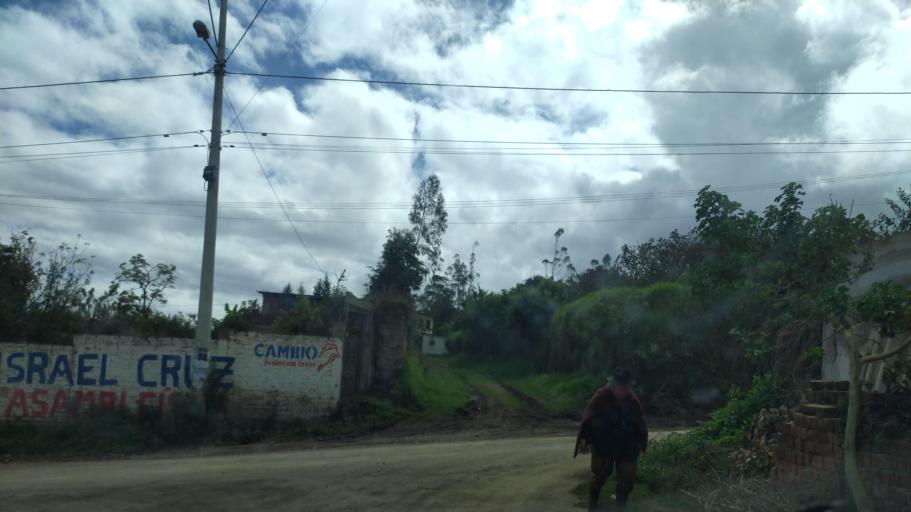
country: EC
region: Chimborazo
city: Guano
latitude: -1.6570
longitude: -78.5659
